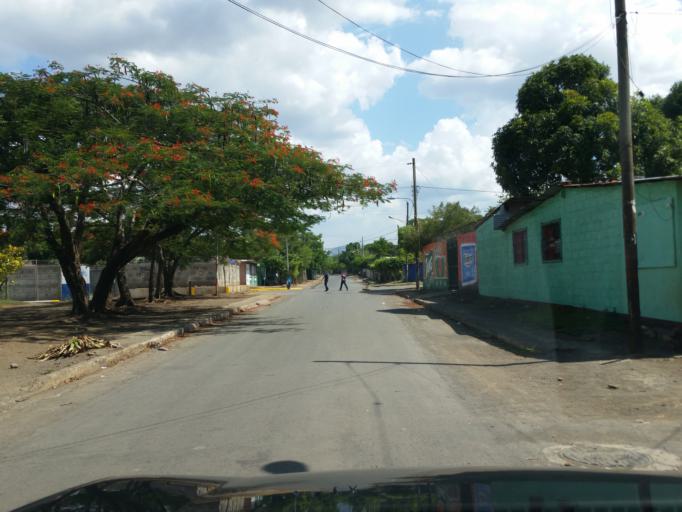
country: NI
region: Managua
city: Managua
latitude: 12.1562
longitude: -86.2074
